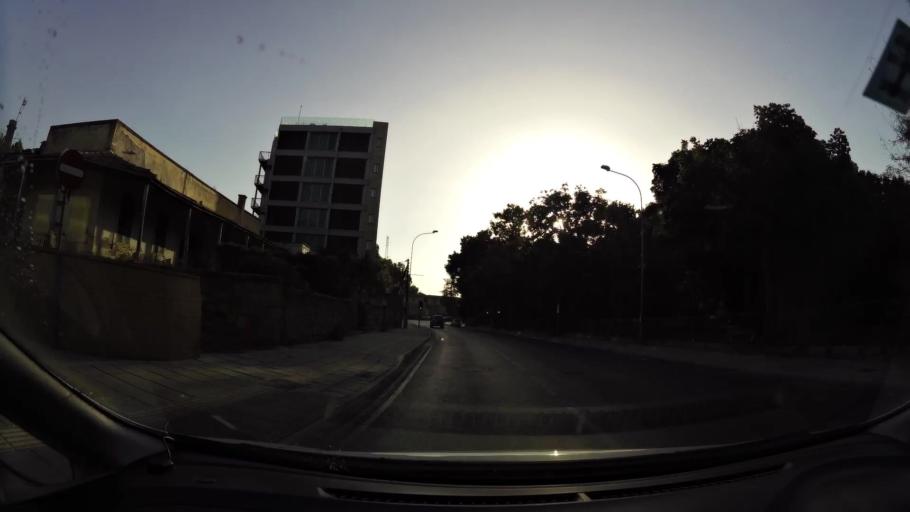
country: CY
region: Lefkosia
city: Nicosia
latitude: 35.1736
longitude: 33.3544
